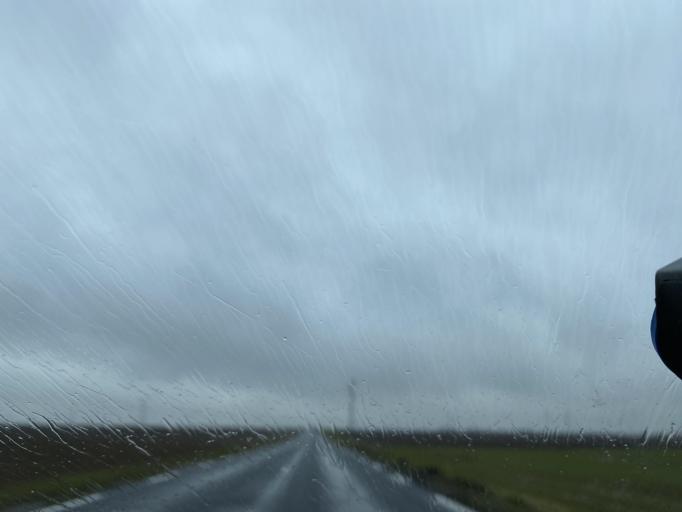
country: FR
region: Centre
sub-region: Departement d'Eure-et-Loir
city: Janville
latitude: 48.1988
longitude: 1.8263
